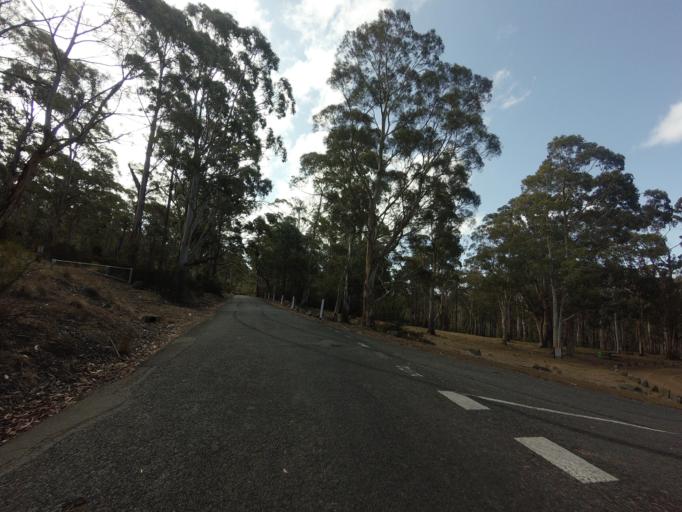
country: AU
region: Tasmania
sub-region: Hobart
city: Dynnyrne
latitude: -42.9229
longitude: 147.2876
